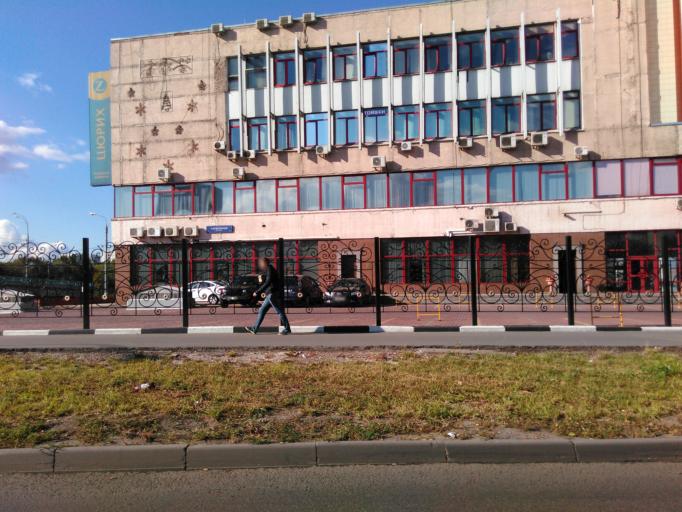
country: RU
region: Moscow
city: Novovladykino
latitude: 55.8487
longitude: 37.5862
